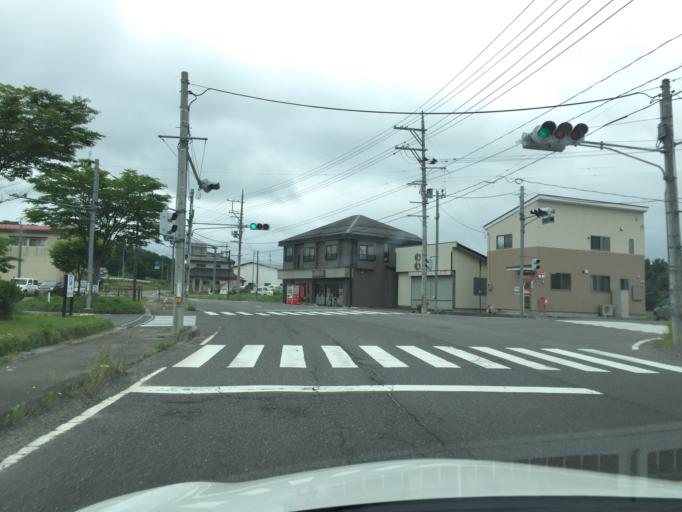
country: JP
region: Fukushima
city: Funehikimachi-funehiki
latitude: 37.4202
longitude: 140.6055
